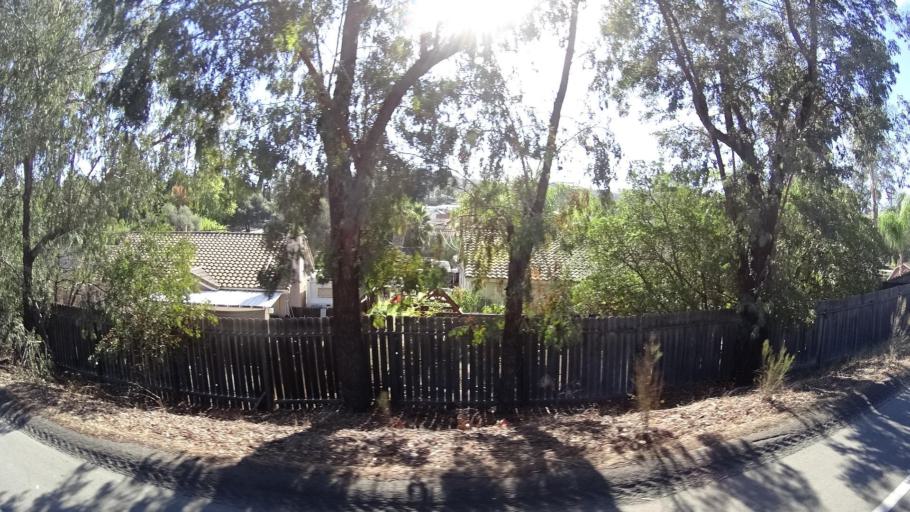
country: US
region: California
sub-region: San Diego County
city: Winter Gardens
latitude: 32.8294
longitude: -116.9082
